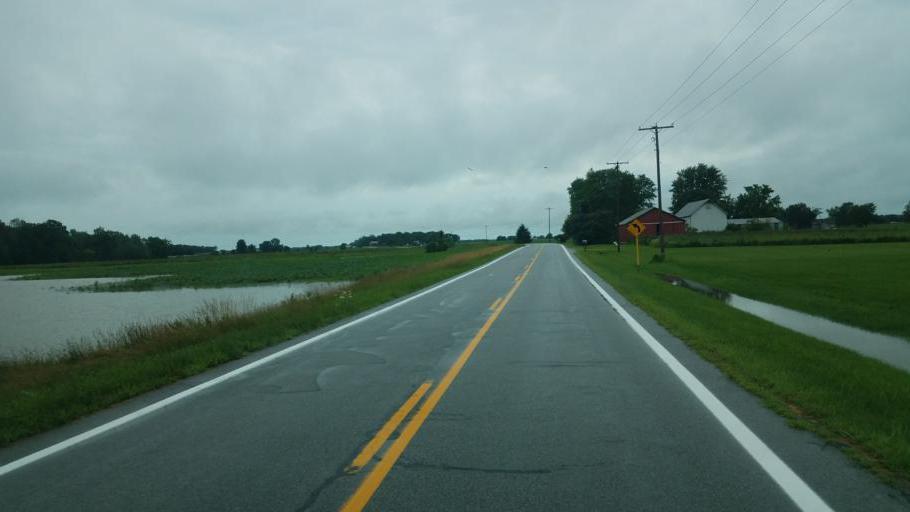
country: US
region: Ohio
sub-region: Union County
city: Richwood
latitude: 40.5034
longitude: -83.2824
